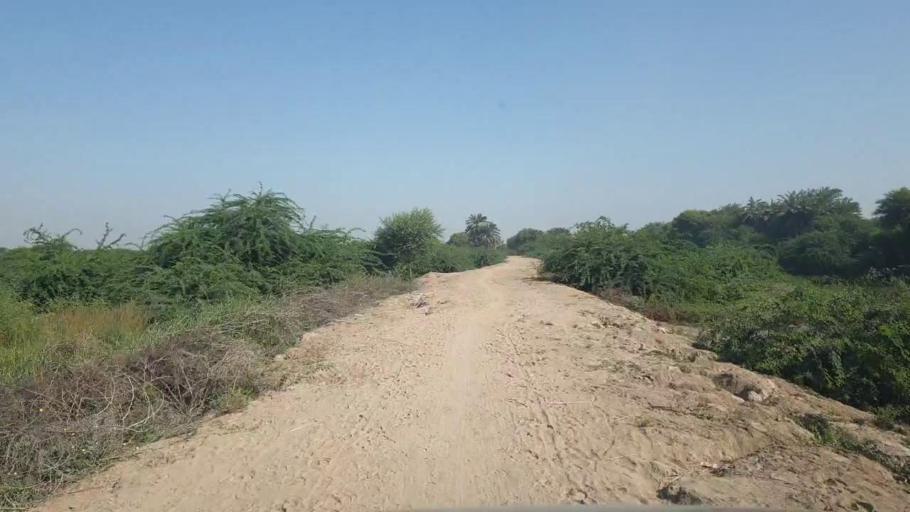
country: PK
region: Sindh
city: Talhar
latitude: 24.7809
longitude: 68.8073
